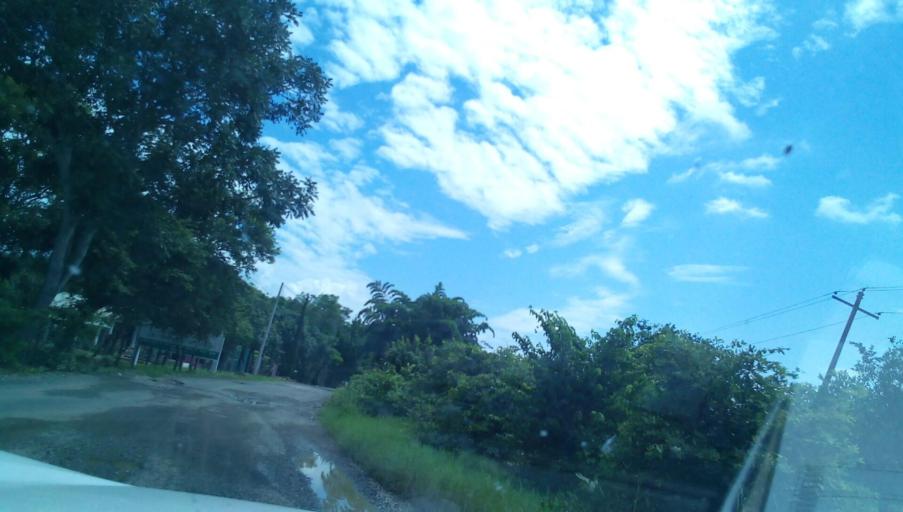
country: MX
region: Veracruz
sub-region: Alamo Temapache
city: Vegas de la Soledad y Soledad Dos
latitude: 20.9070
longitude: -97.9288
